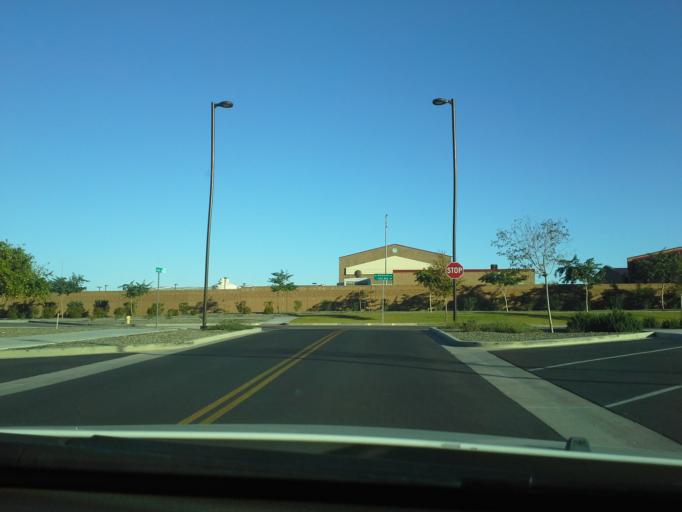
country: US
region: Arizona
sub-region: Maricopa County
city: Tempe
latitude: 33.4324
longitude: -111.8802
